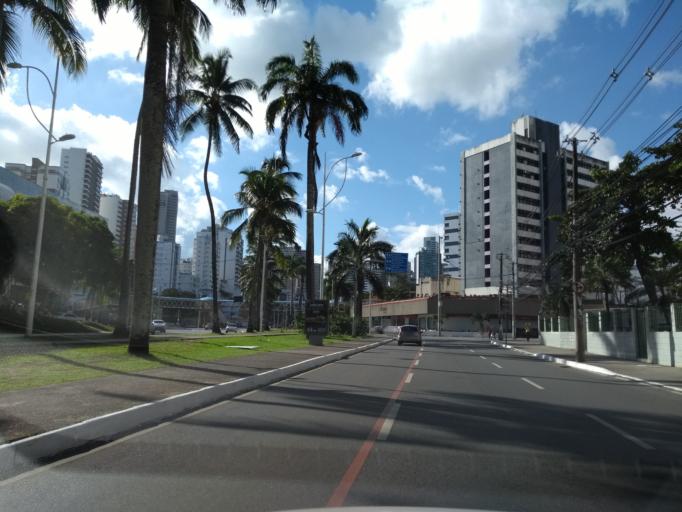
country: BR
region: Bahia
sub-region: Salvador
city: Salvador
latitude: -13.0071
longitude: -38.5231
